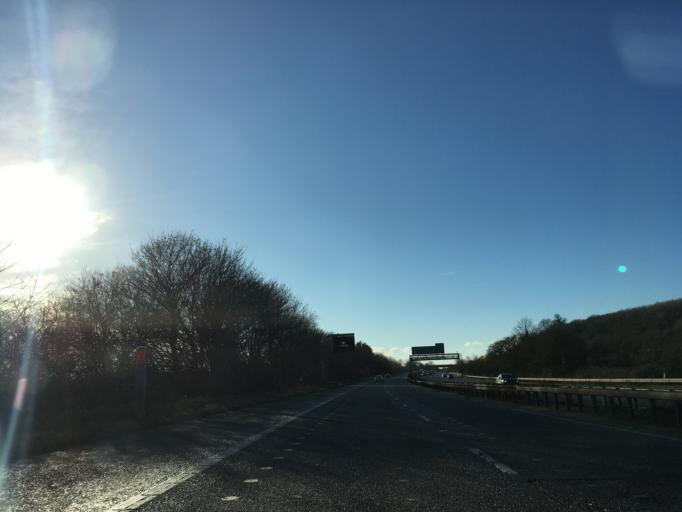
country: GB
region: England
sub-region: South Gloucestershire
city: Stoke Gifford
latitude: 51.4981
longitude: -2.5325
